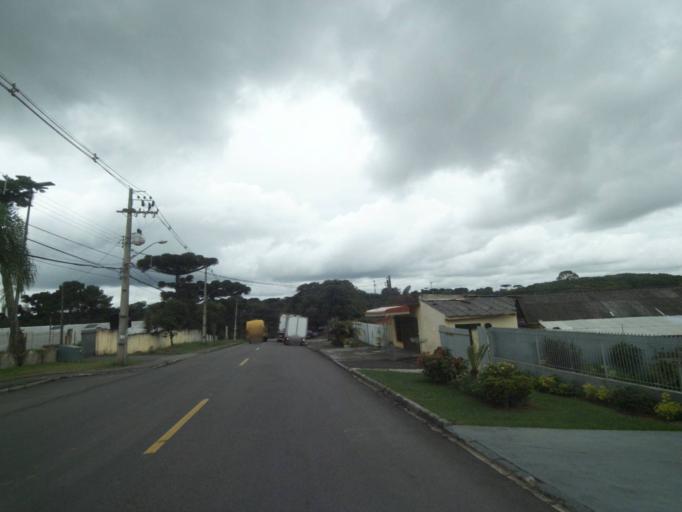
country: BR
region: Parana
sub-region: Curitiba
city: Curitiba
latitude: -25.4560
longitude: -49.3257
